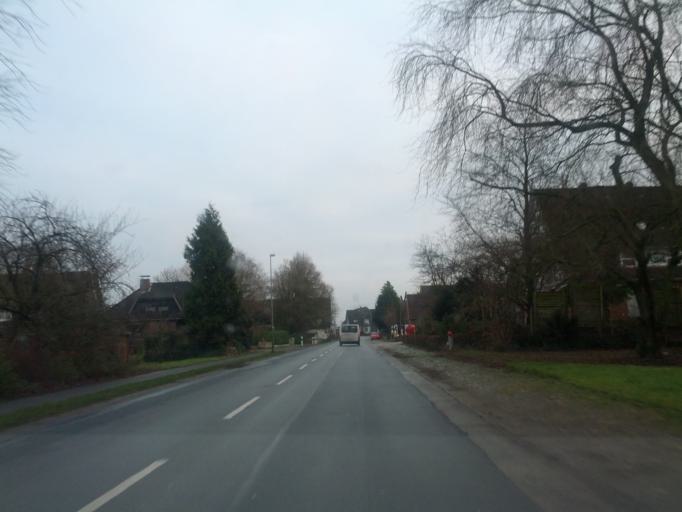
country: DE
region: Lower Saxony
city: Jork
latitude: 53.5266
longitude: 9.7051
